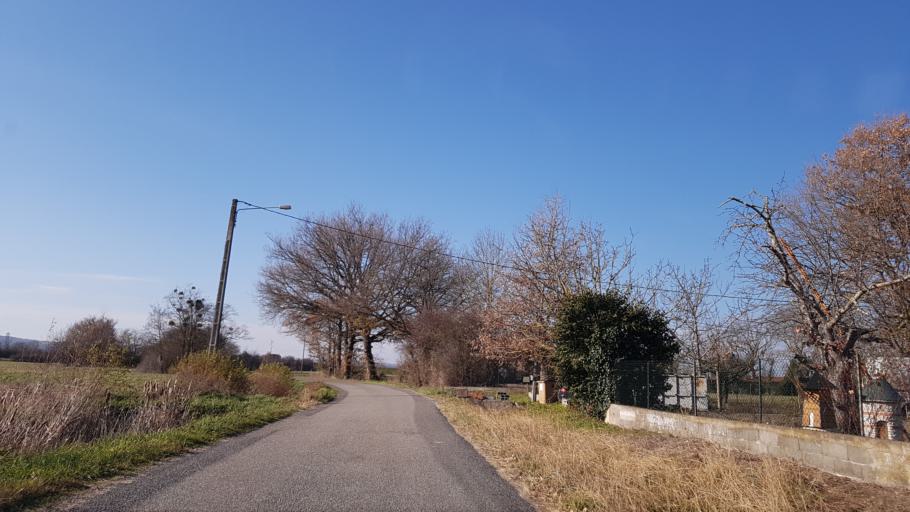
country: FR
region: Midi-Pyrenees
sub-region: Departement de l'Ariege
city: Mazeres
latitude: 43.1842
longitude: 1.6426
